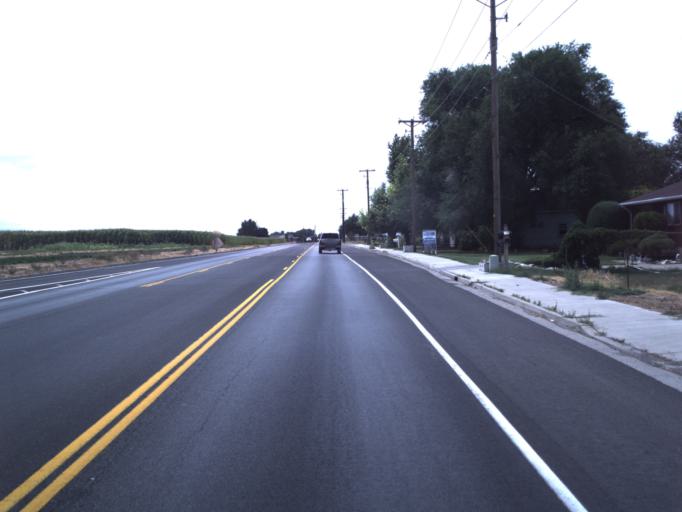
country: US
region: Utah
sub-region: Davis County
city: Clinton
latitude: 41.1321
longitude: -112.0646
